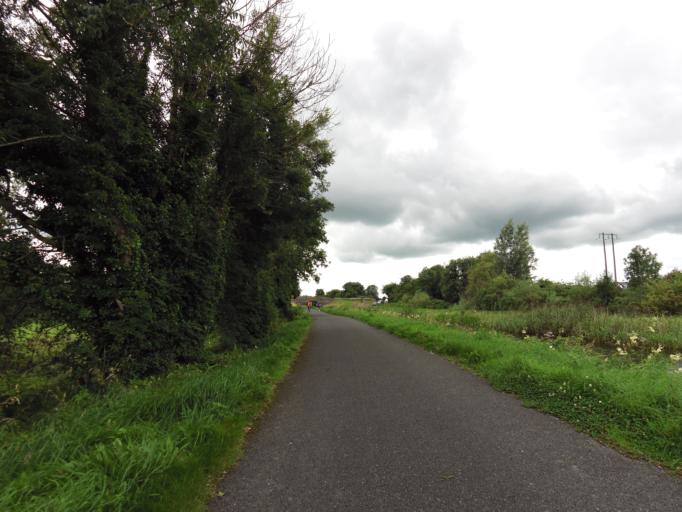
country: IE
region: Leinster
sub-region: An Iarmhi
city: An Muileann gCearr
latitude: 53.5107
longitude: -7.3850
